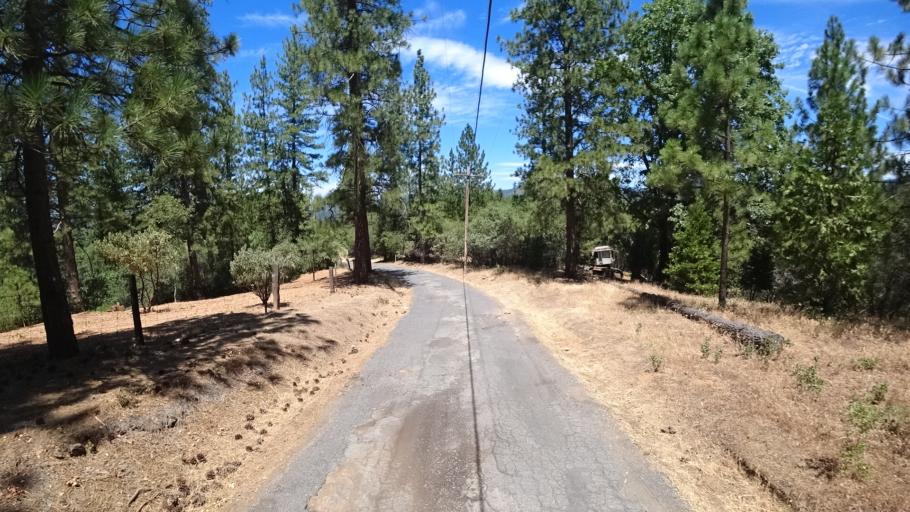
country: US
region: California
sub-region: Calaveras County
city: Forest Meadows
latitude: 38.2072
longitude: -120.4630
